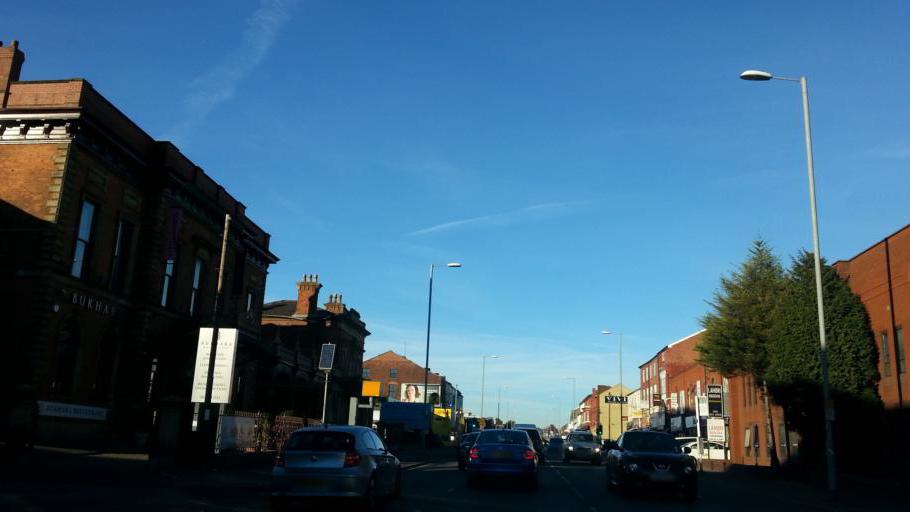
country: GB
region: England
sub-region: Manchester
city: Cheetham Hill
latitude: 53.4933
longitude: -2.2398
